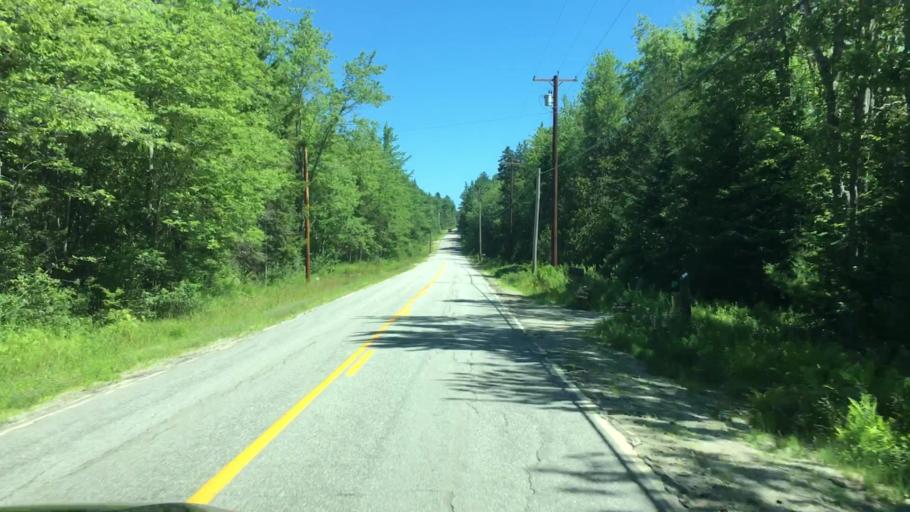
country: US
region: Maine
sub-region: Hancock County
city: Penobscot
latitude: 44.5051
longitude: -68.6776
